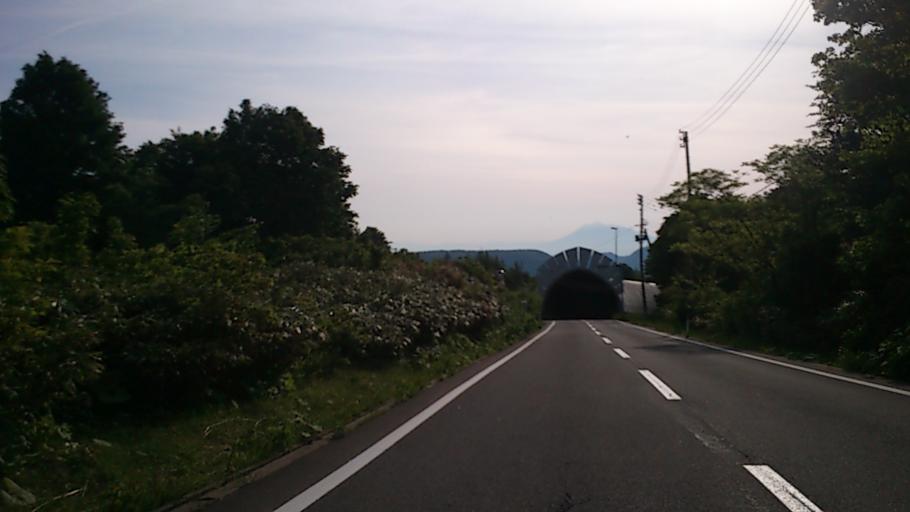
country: JP
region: Aomori
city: Aomori Shi
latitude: 40.6420
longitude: 140.8109
